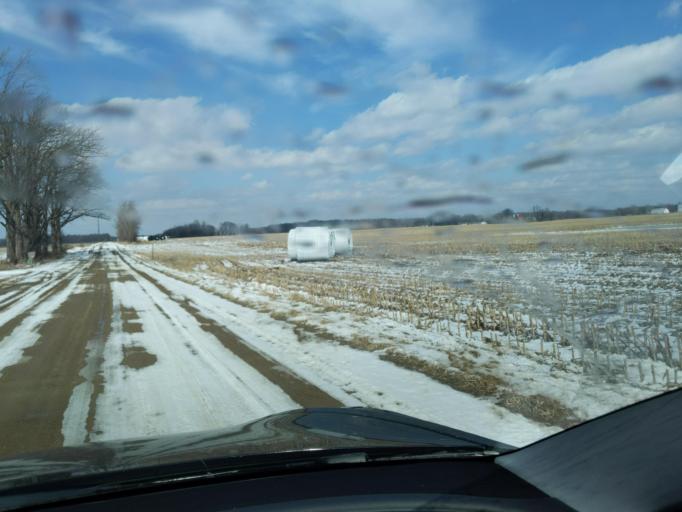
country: US
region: Michigan
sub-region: Livingston County
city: Fowlerville
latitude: 42.6297
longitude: -84.0620
